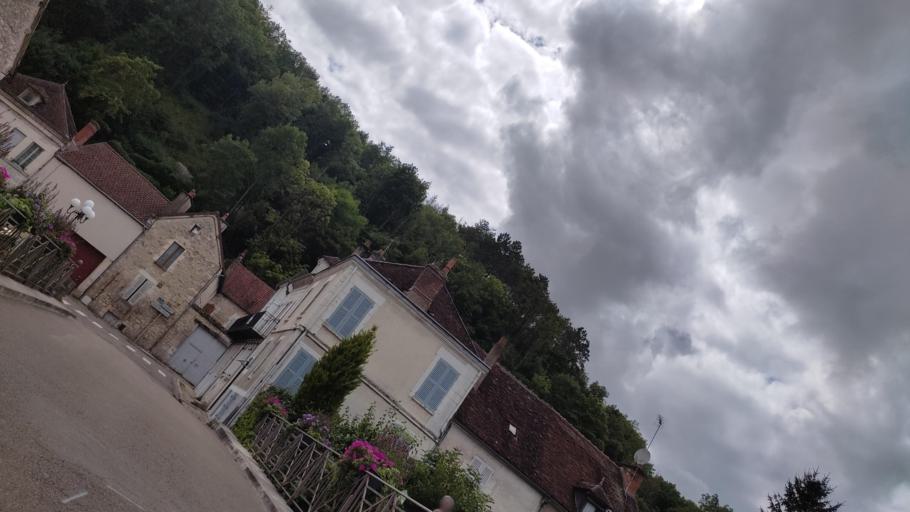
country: FR
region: Bourgogne
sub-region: Departement de l'Yonne
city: Tonnerre
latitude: 47.8595
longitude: 3.9688
